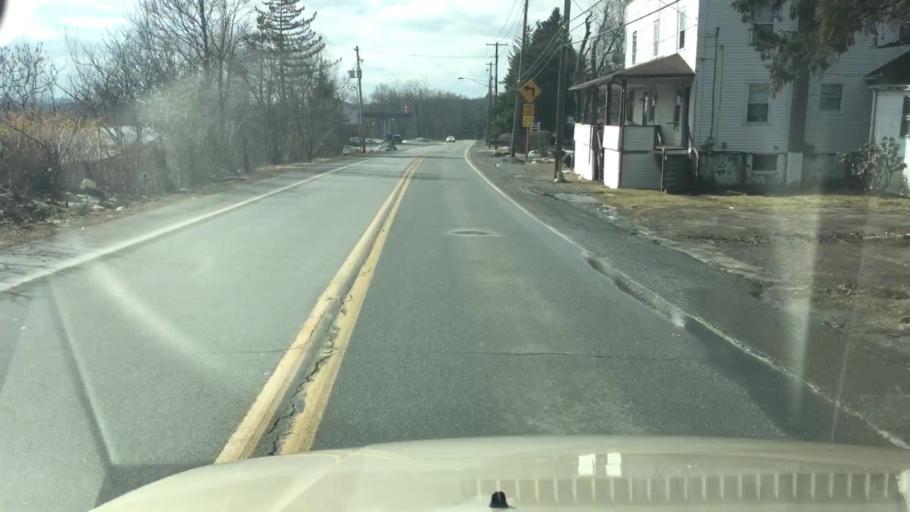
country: US
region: Pennsylvania
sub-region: Luzerne County
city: Freeland
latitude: 41.0077
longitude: -75.9041
